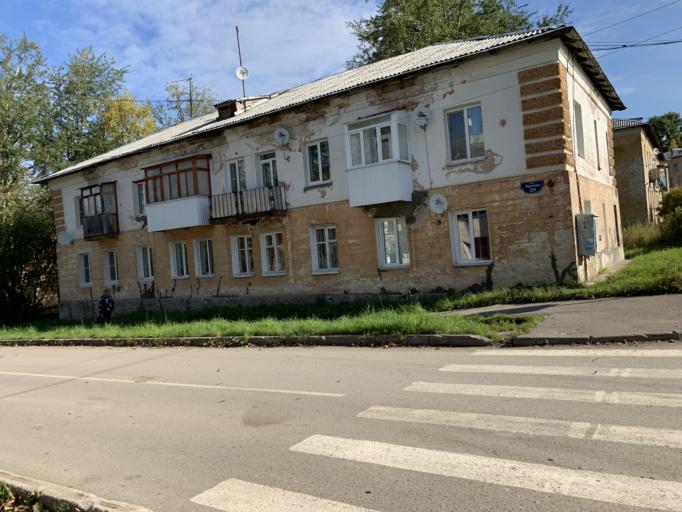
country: RU
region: Perm
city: Gubakha
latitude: 58.8406
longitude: 57.5549
